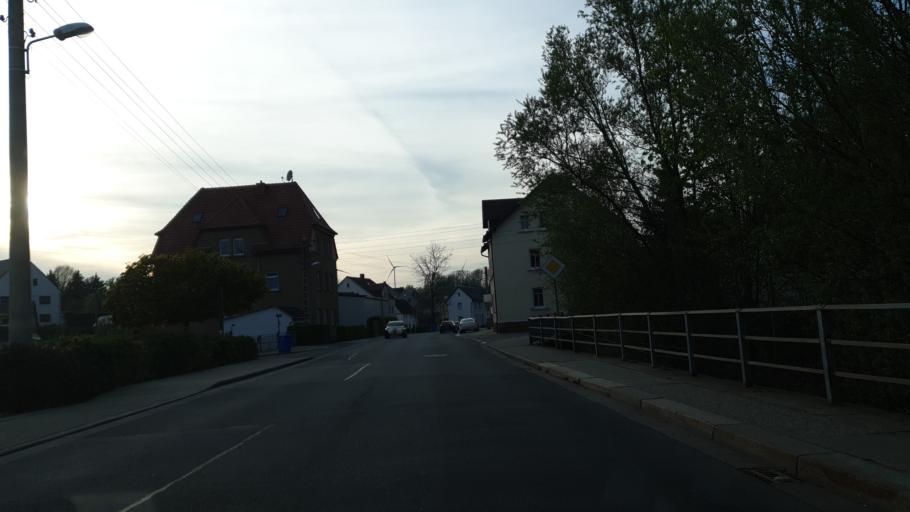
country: DE
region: Saxony
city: Gersdorf
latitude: 50.7510
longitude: 12.7111
